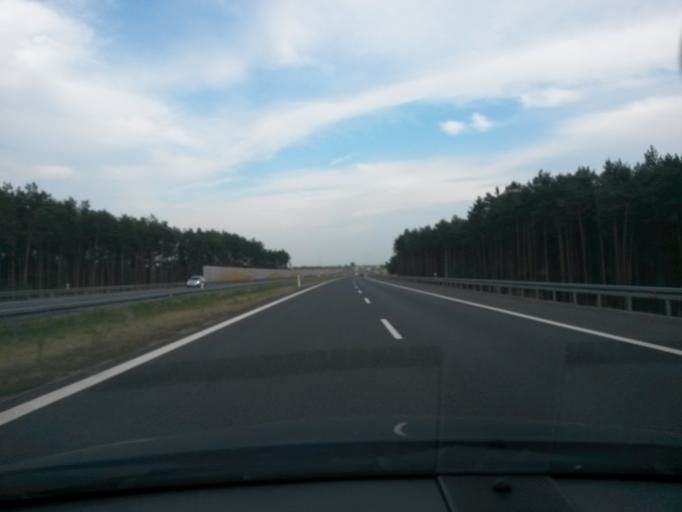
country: PL
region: Lodz Voivodeship
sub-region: Powiat leczycki
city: Swinice Warckie
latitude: 52.0253
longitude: 18.9179
